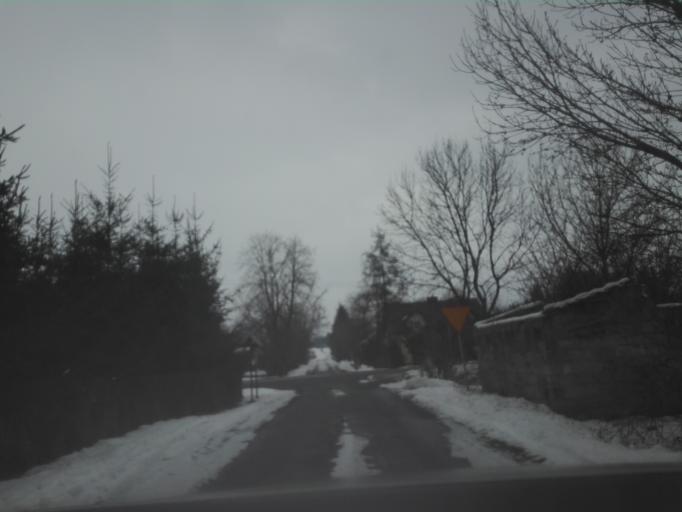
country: PL
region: Lublin Voivodeship
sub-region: Powiat hrubieszowski
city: Horodlo
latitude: 50.8427
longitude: 24.0116
